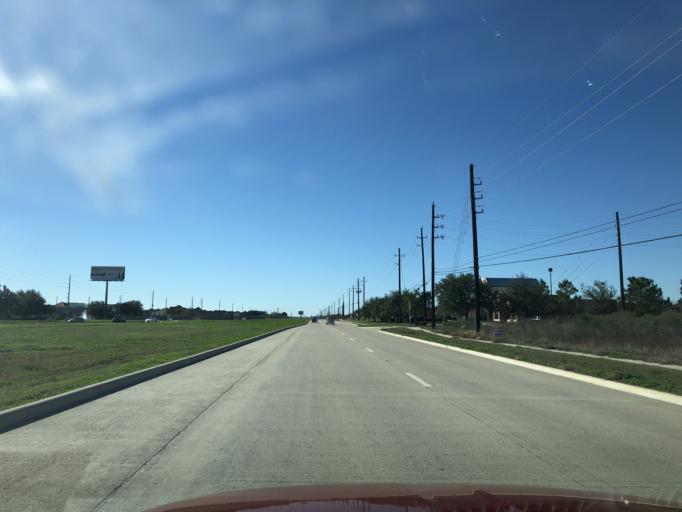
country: US
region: Texas
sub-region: Fort Bend County
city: Fulshear
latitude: 29.6965
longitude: -95.8254
